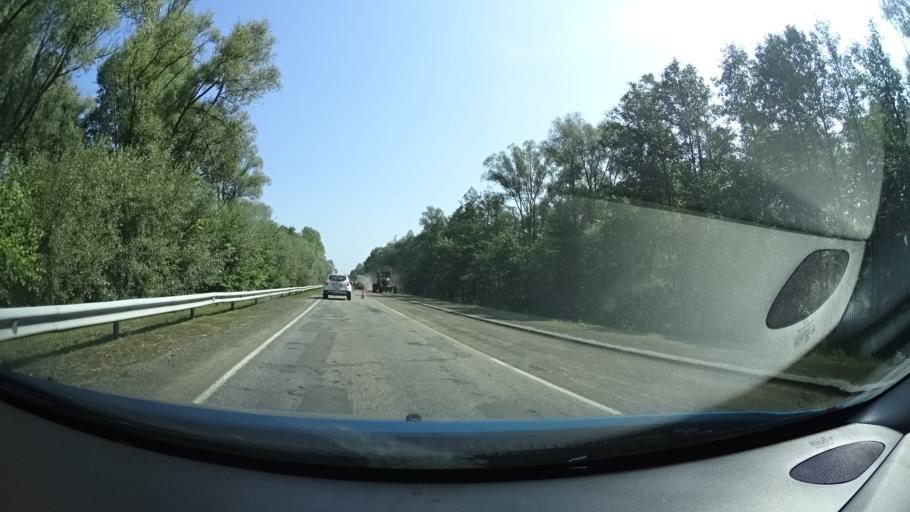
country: RU
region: Bashkortostan
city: Ulukulevo
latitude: 54.4543
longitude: 56.5059
